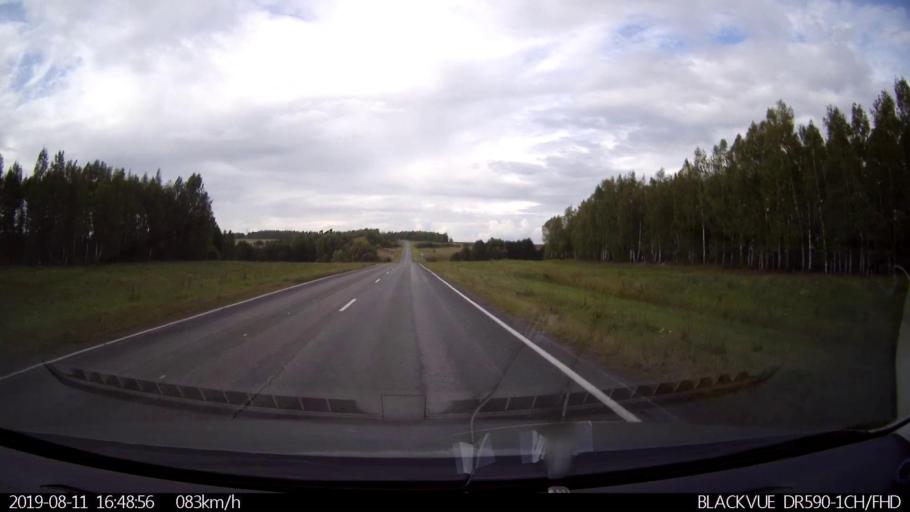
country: RU
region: Ulyanovsk
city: Mayna
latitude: 54.2151
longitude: 47.6941
